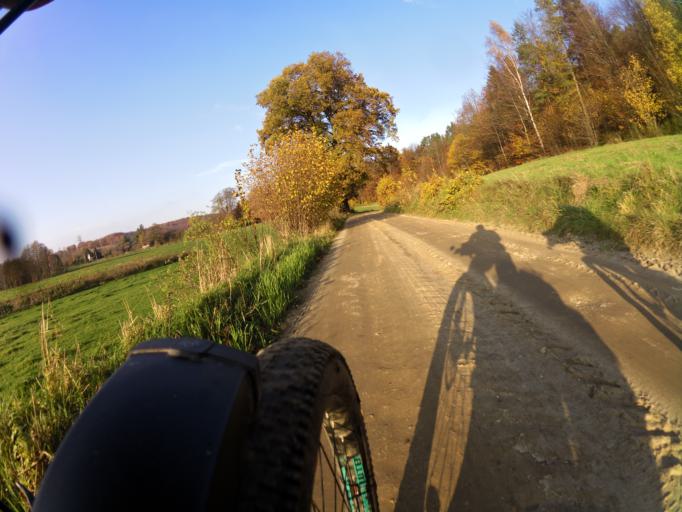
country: PL
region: Pomeranian Voivodeship
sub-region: Powiat pucki
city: Krokowa
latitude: 54.7480
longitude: 18.1955
